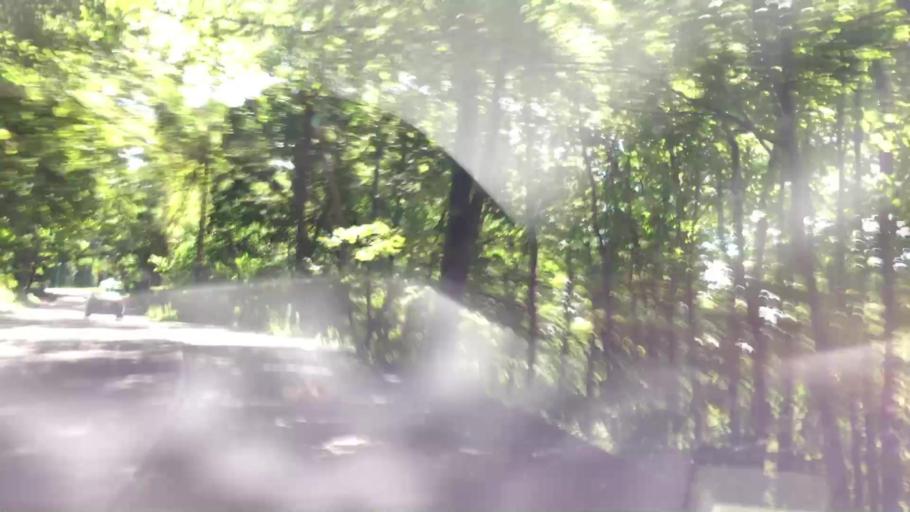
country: US
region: Pennsylvania
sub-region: Allegheny County
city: South Park Township
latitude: 40.2945
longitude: -79.9920
